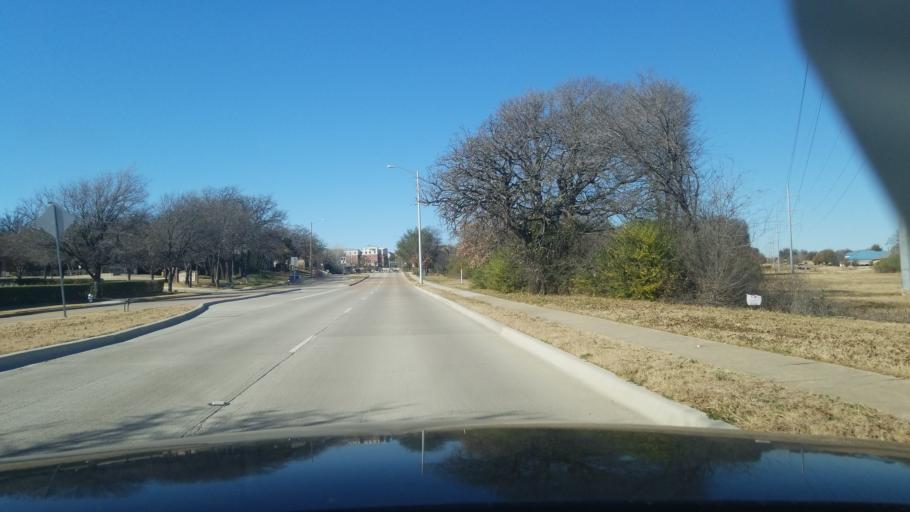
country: US
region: Texas
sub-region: Denton County
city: Corinth
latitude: 33.1810
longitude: -97.0941
